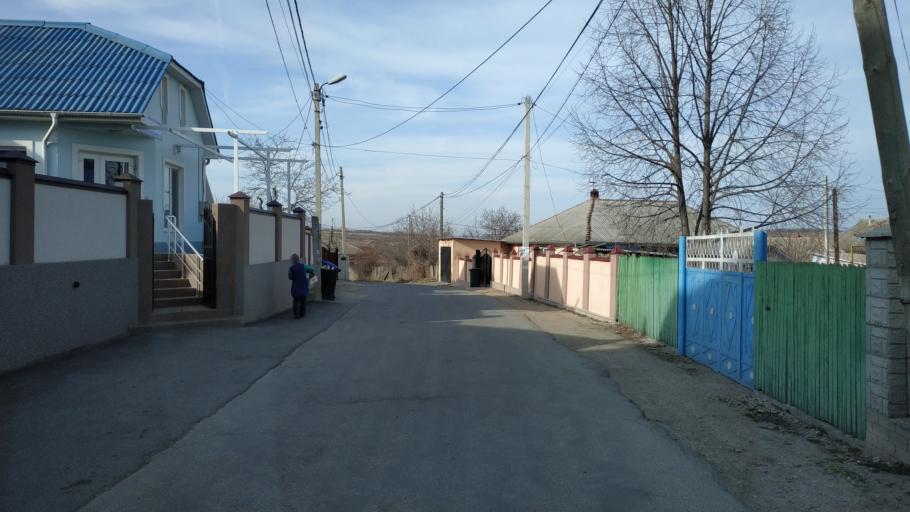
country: MD
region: Chisinau
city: Vatra
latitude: 47.0738
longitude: 28.6717
